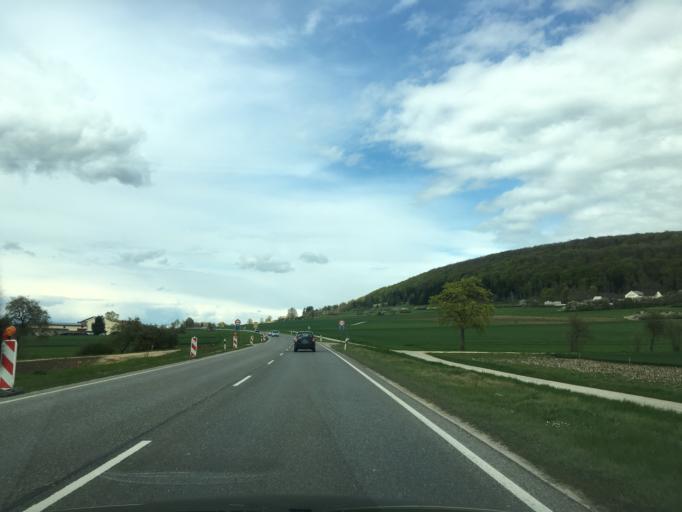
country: DE
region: Bavaria
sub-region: Regierungsbezirk Mittelfranken
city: Weissenburg in Bayern
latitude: 48.9960
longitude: 10.9507
